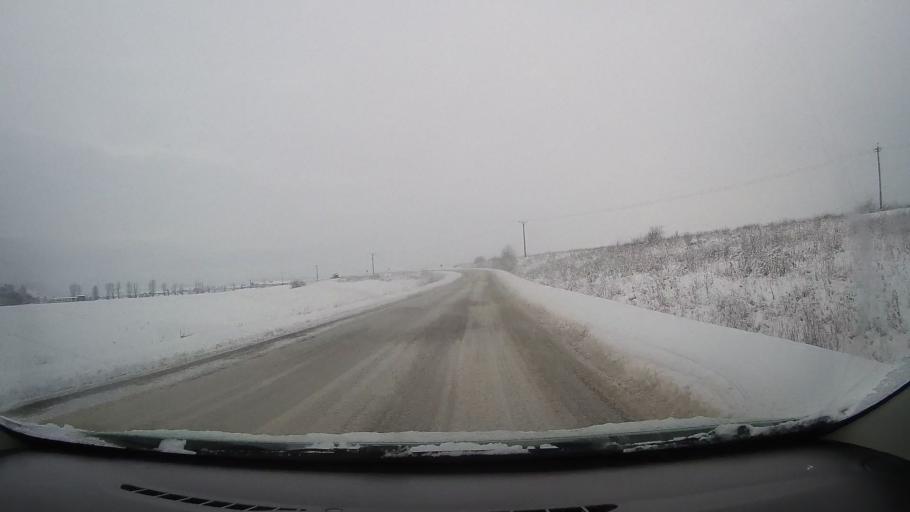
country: RO
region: Alba
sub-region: Comuna Pianu
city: Pianu de Jos
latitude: 45.9661
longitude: 23.4795
